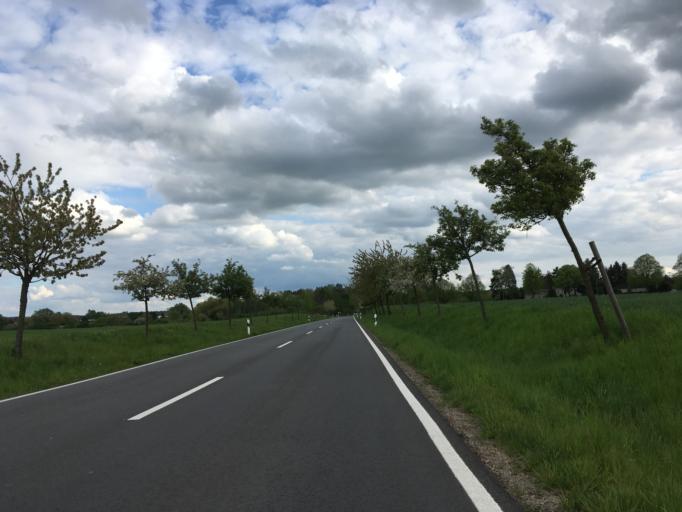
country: DE
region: Brandenburg
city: Bernau bei Berlin
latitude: 52.6485
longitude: 13.6060
